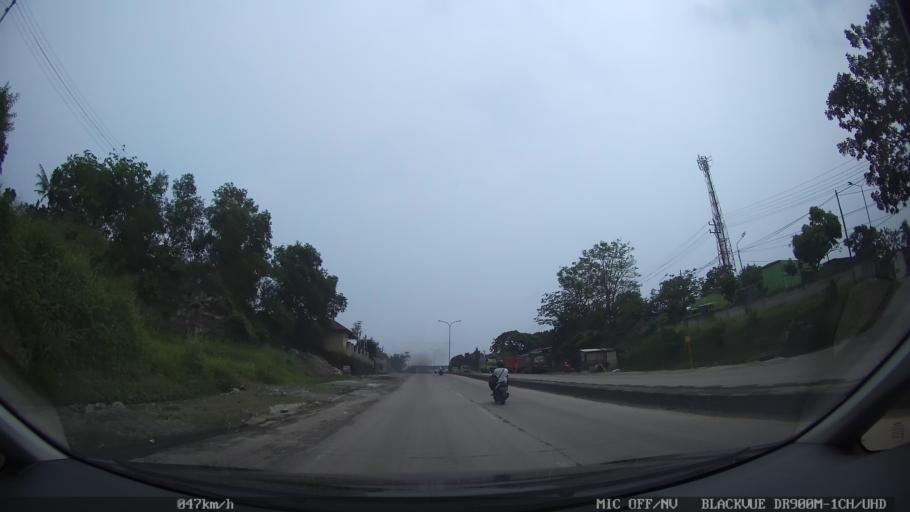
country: ID
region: Lampung
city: Bandarlampung
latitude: -5.4246
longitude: 105.2960
